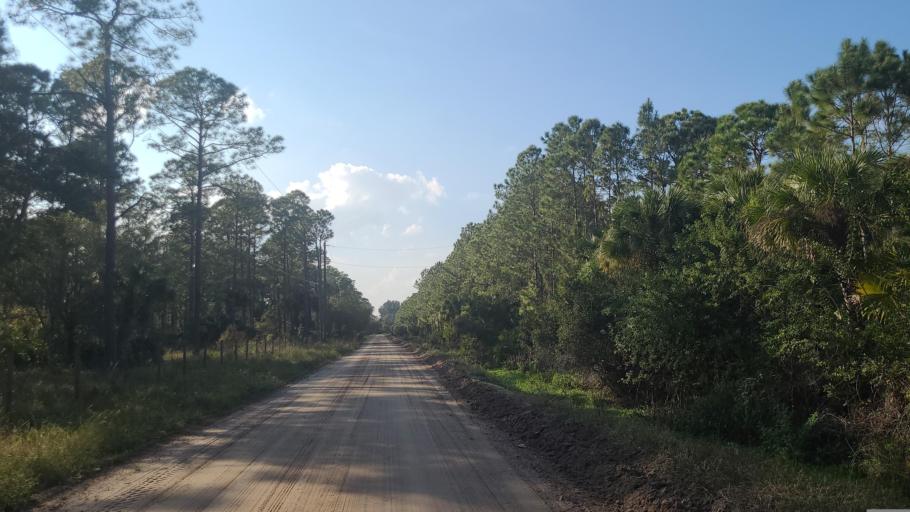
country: US
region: Florida
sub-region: Indian River County
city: Fellsmere
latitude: 27.7539
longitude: -80.6094
